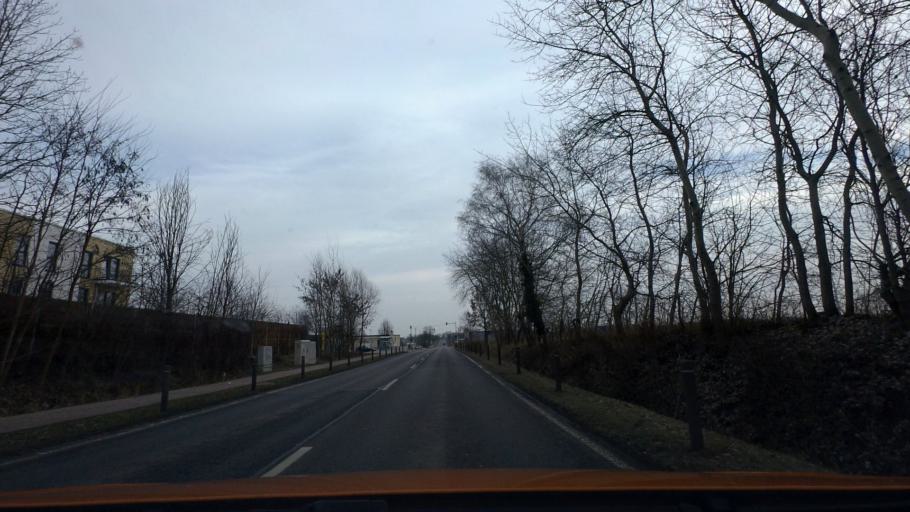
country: DE
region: Berlin
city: Buch
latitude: 52.6295
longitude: 13.5263
